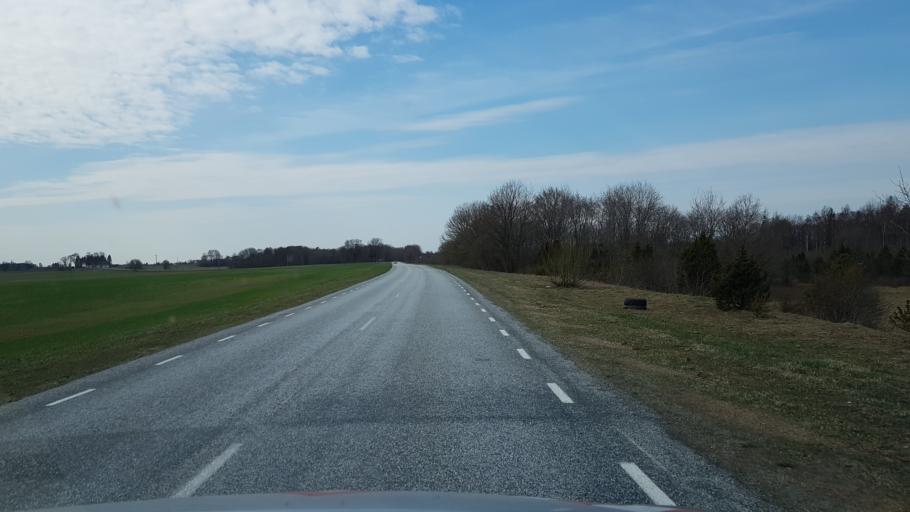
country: EE
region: Laeaene-Virumaa
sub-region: Haljala vald
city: Haljala
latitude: 59.4726
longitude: 26.1703
